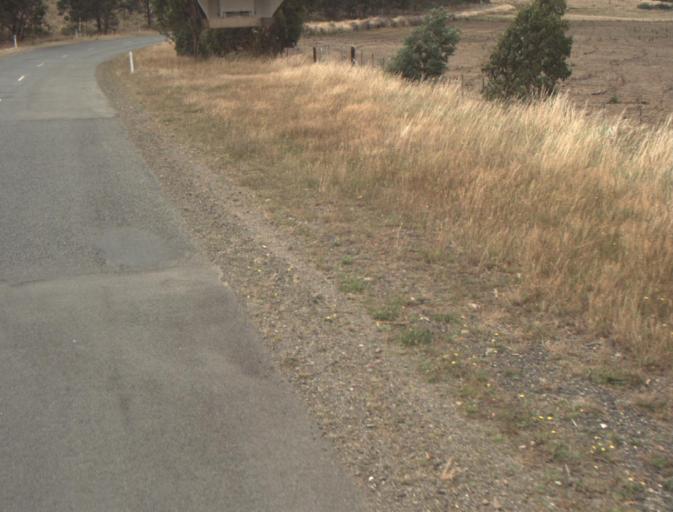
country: AU
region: Tasmania
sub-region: Northern Midlands
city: Evandale
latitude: -41.5068
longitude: 147.3738
